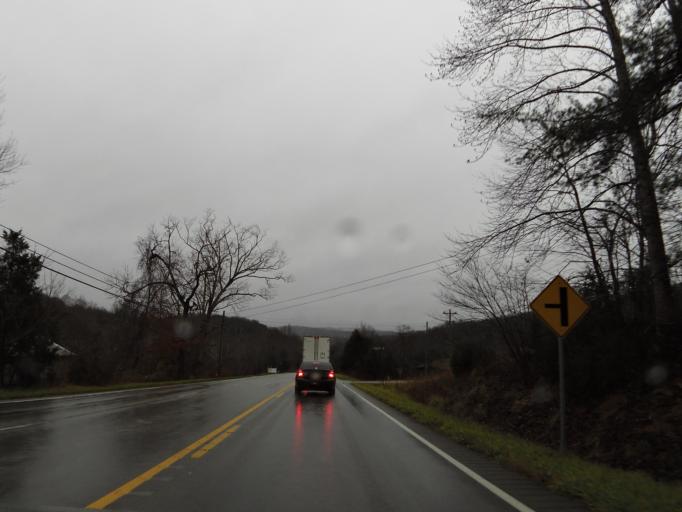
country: US
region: Kentucky
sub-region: Rockcastle County
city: Mount Vernon
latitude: 37.4016
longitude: -84.3350
